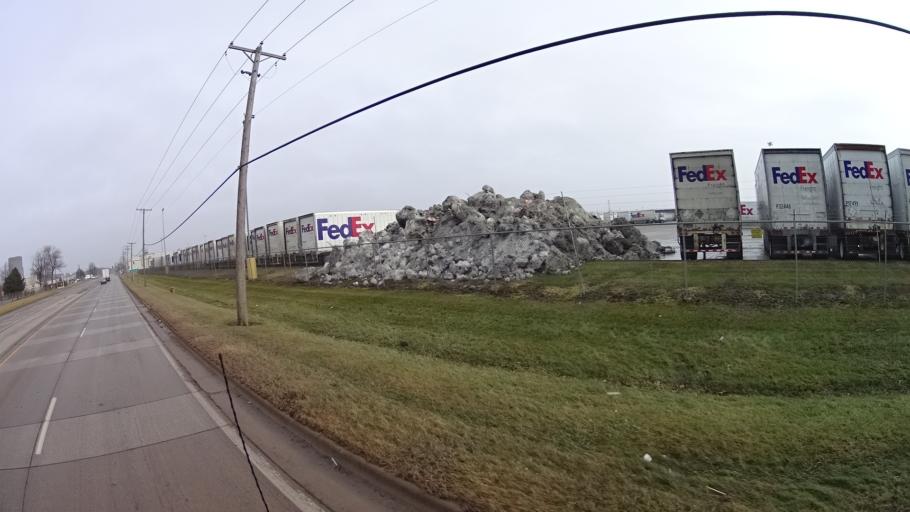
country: US
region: Illinois
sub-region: Cook County
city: Chicago Heights
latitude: 41.5181
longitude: -87.6162
